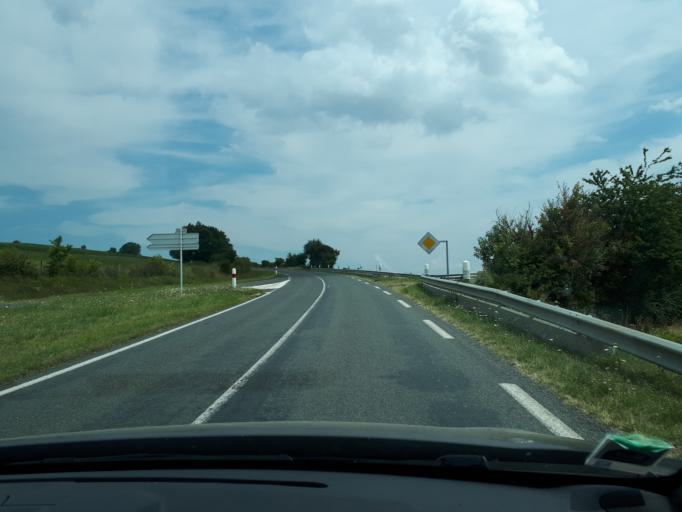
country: FR
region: Centre
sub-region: Departement du Cher
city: Rians
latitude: 47.2347
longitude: 2.6455
